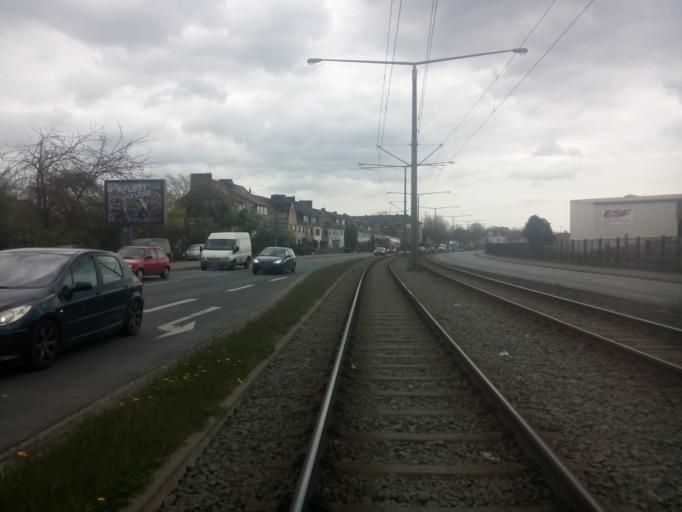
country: DE
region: Bremen
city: Bremen
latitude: 53.1104
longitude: 8.7582
